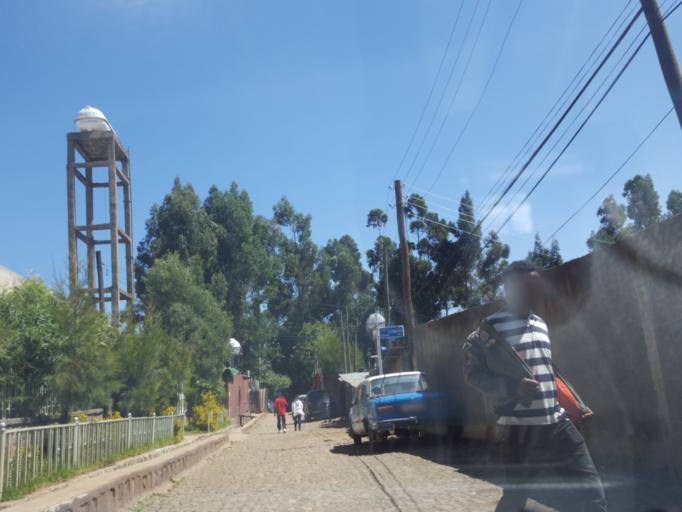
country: ET
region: Adis Abeba
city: Addis Ababa
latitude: 9.0642
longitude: 38.7469
